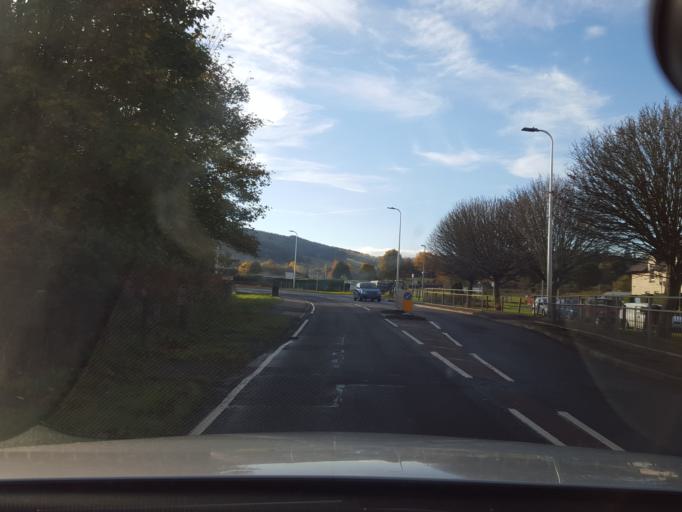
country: GB
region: Scotland
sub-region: Highland
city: Beauly
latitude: 57.3329
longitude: -4.4808
